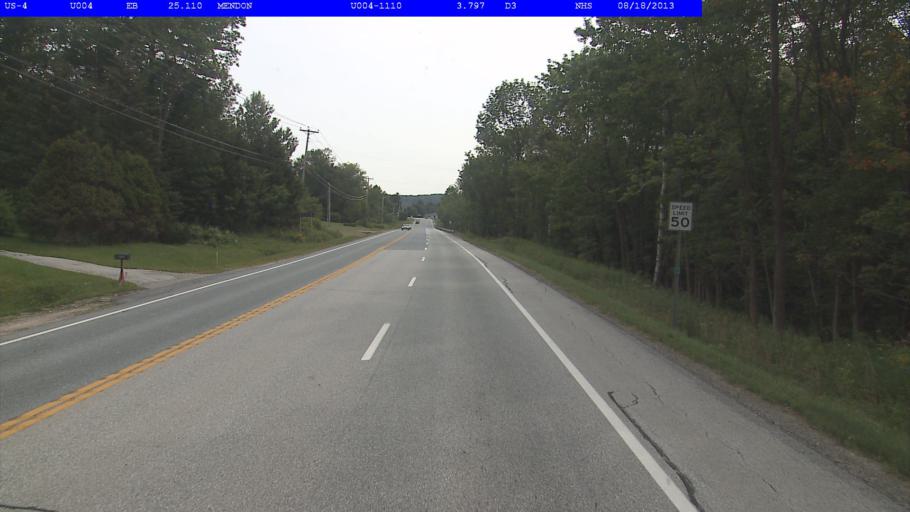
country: US
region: Vermont
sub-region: Rutland County
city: Rutland
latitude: 43.6555
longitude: -72.8817
